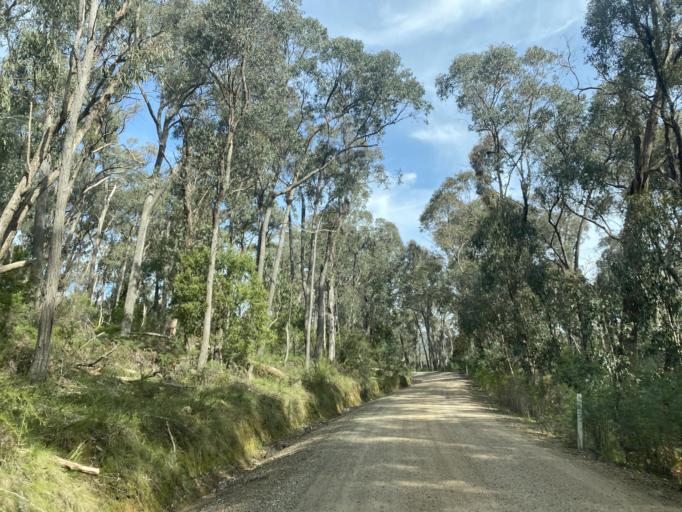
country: AU
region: Victoria
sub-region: Mansfield
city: Mansfield
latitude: -36.8289
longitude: 146.1586
